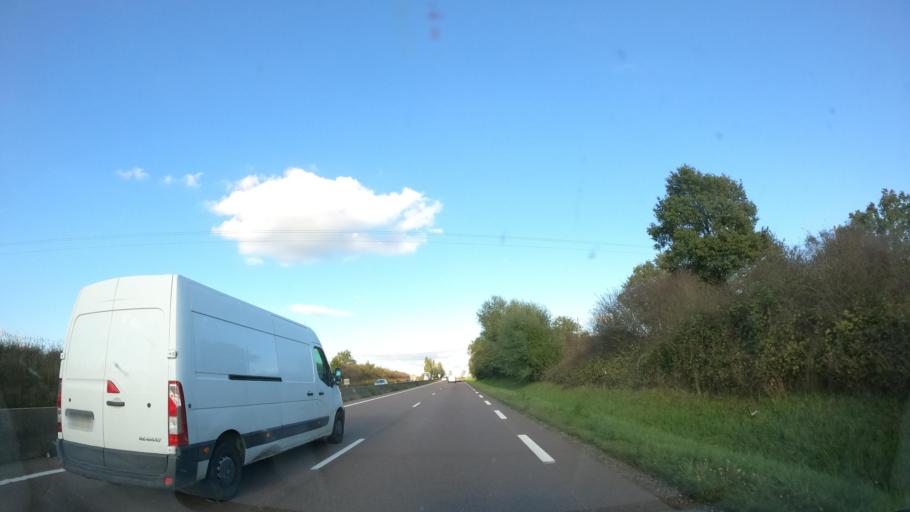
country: FR
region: Bourgogne
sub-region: Departement de Saone-et-Loire
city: Ciry-le-Noble
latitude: 46.6211
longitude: 4.2911
